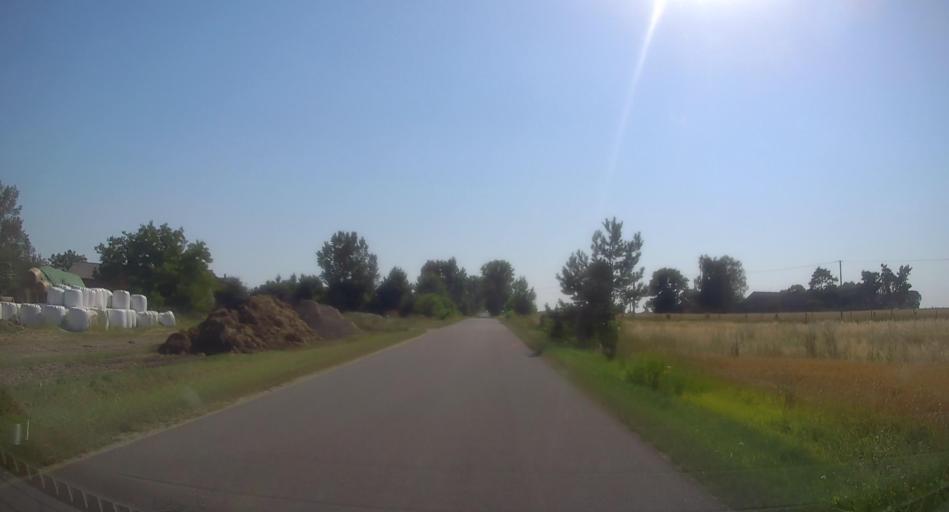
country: PL
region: Lodz Voivodeship
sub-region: Powiat skierniewicki
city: Kaweczyn Nowy
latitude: 51.8772
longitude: 20.2133
